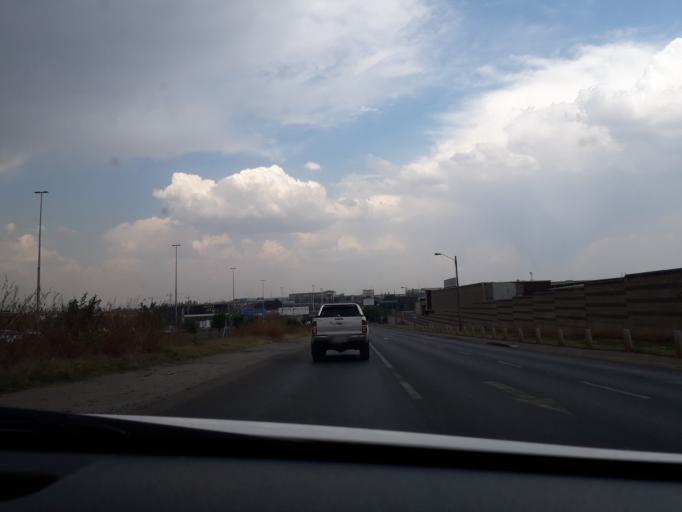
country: ZA
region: Gauteng
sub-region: City of Johannesburg Metropolitan Municipality
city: Modderfontein
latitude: -26.1298
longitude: 28.2138
